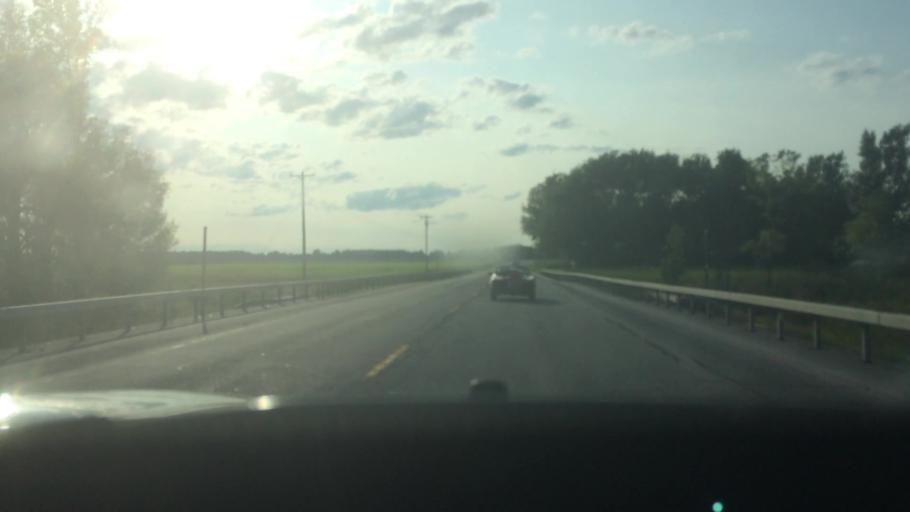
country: US
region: New York
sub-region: St. Lawrence County
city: Ogdensburg
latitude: 44.6607
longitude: -75.3350
